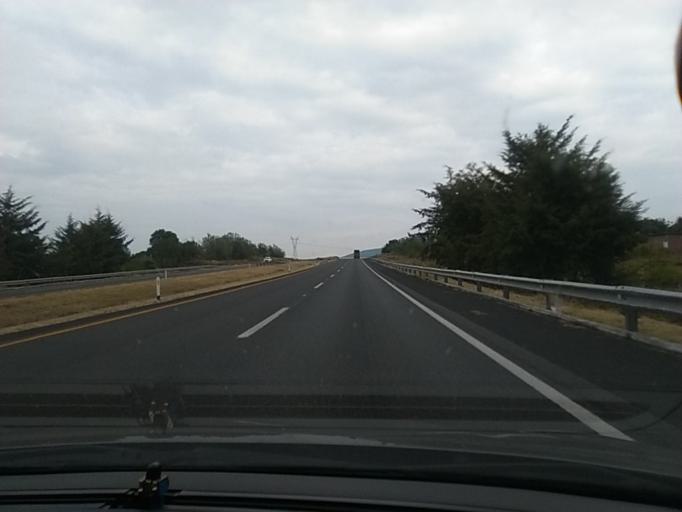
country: MX
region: Michoacan
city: Panindicuaro de la Reforma
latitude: 19.9902
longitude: -101.8025
